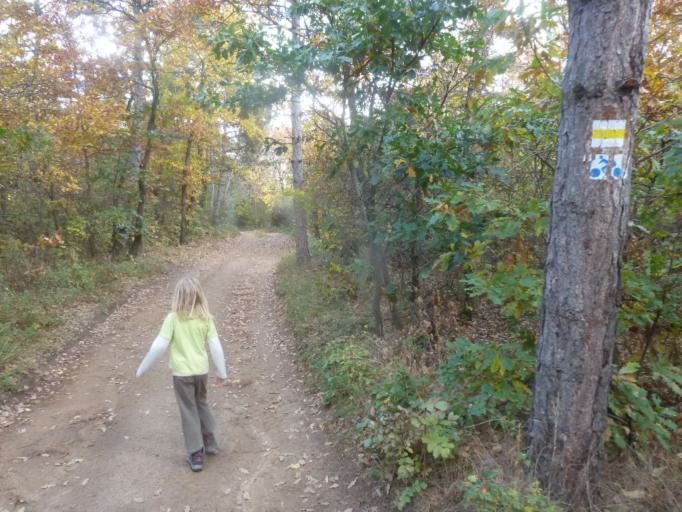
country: HU
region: Fejer
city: Pakozd
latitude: 47.2263
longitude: 18.5473
